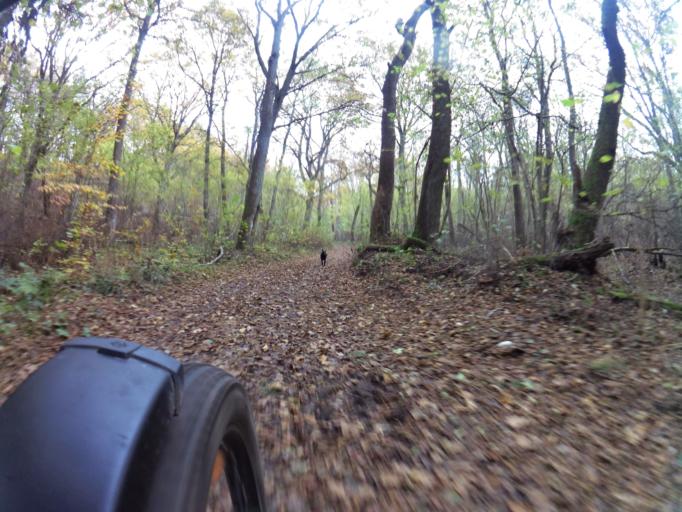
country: PL
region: Pomeranian Voivodeship
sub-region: Powiat pucki
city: Krokowa
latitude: 54.8305
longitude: 18.1099
